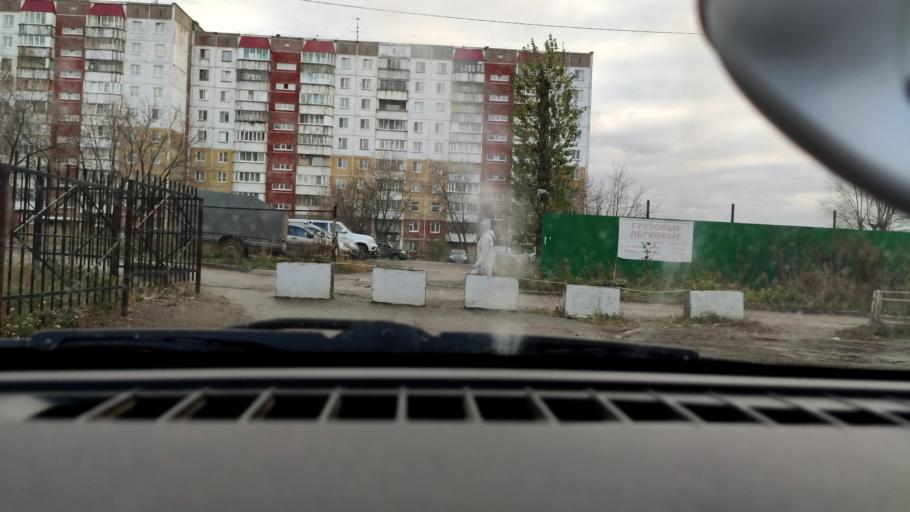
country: RU
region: Perm
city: Perm
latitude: 57.9704
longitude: 56.2251
